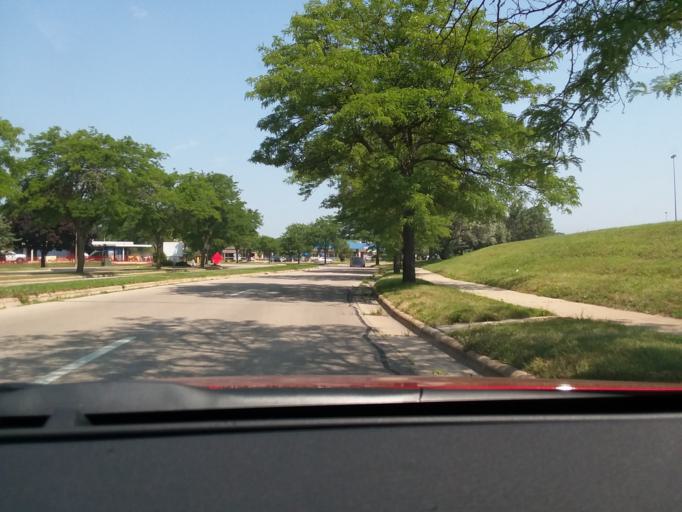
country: US
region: Wisconsin
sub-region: Dane County
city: Monona
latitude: 43.1236
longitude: -89.3085
